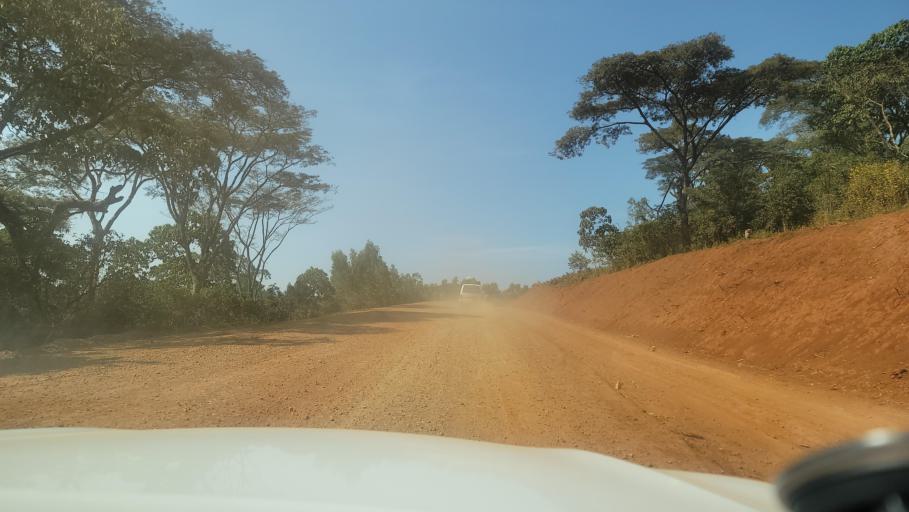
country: ET
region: Oromiya
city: Agaro
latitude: 7.8174
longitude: 36.5235
